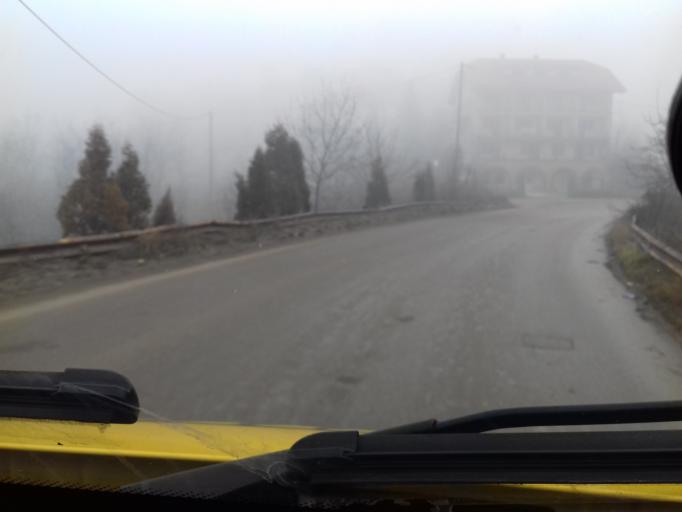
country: BA
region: Federation of Bosnia and Herzegovina
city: Kakanj
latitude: 44.1279
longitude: 18.1052
